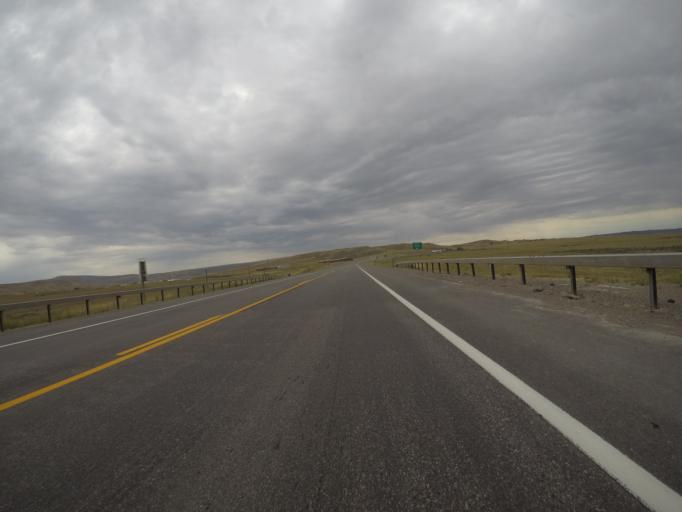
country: US
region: Wyoming
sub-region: Lincoln County
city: Kemmerer
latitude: 41.7941
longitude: -110.5822
